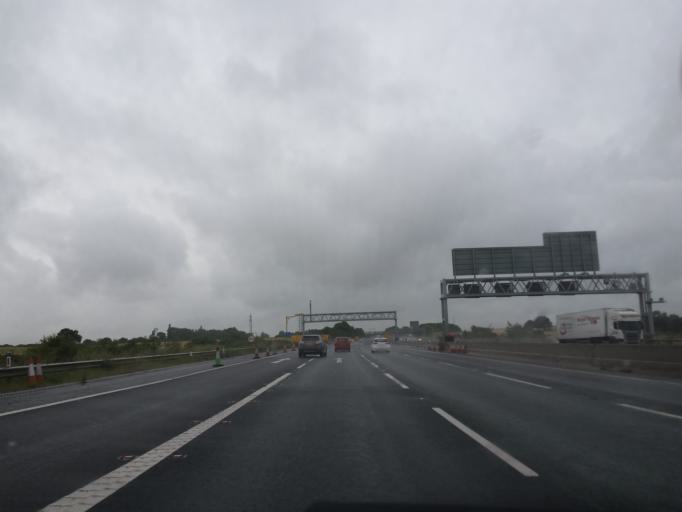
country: GB
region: England
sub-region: Rotherham
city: Ulley
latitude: 53.3785
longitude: -1.2788
